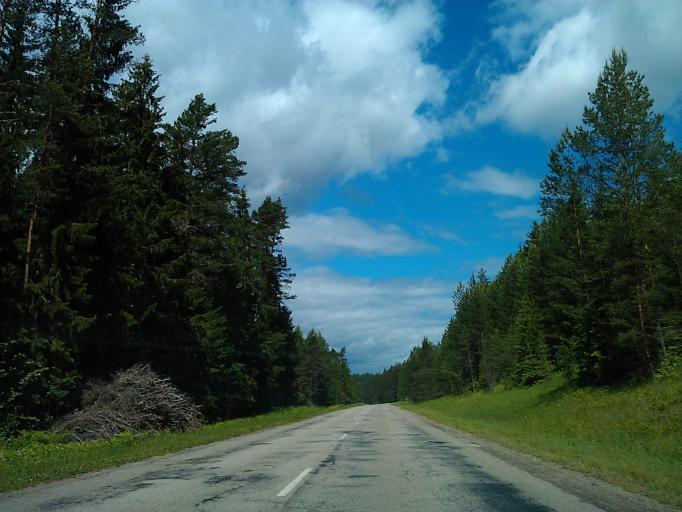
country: LV
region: Talsu Rajons
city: Sabile
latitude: 57.0756
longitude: 22.5317
